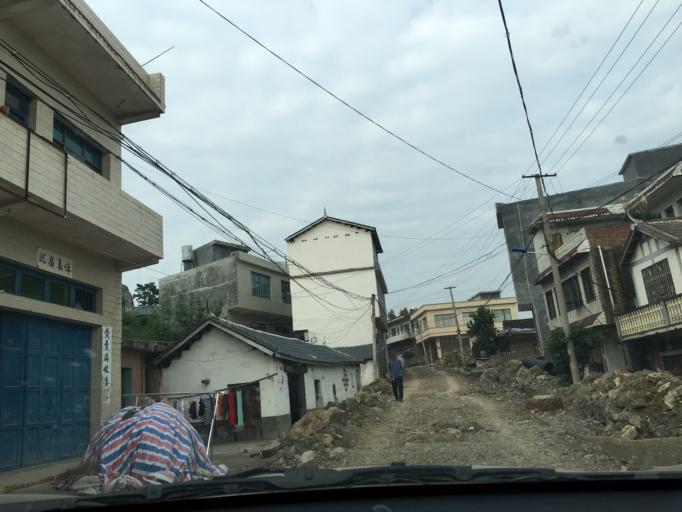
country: CN
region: Guangxi Zhuangzu Zizhiqu
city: Xinzhou
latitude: 25.4602
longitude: 105.4894
